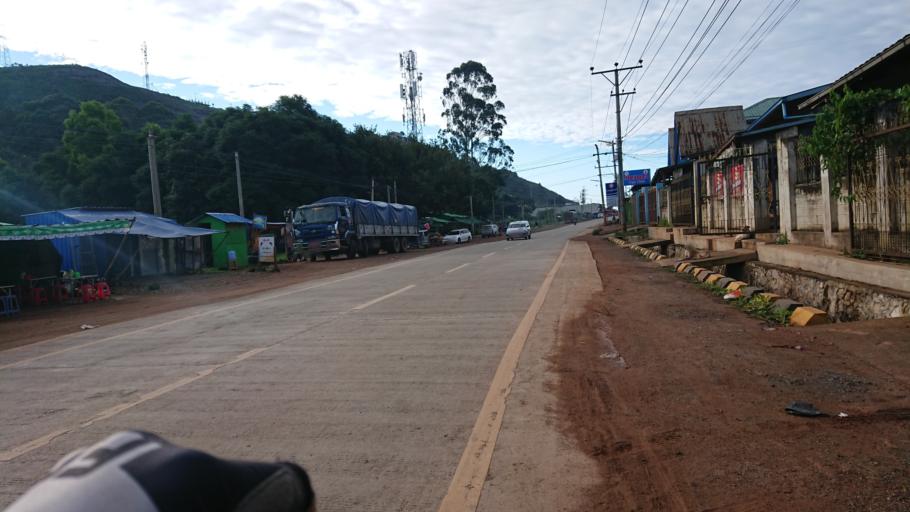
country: MM
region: Shan
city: Taunggyi
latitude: 20.7478
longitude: 97.0500
